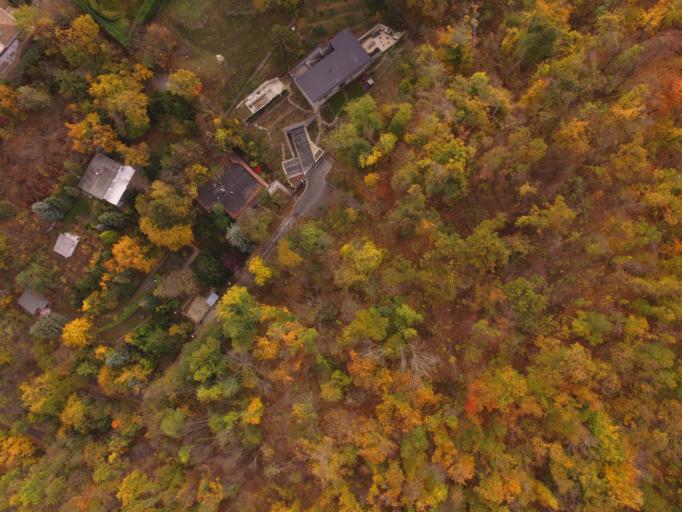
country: HU
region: Budapest
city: Budapest XII. keruelet
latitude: 47.5052
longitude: 18.9720
